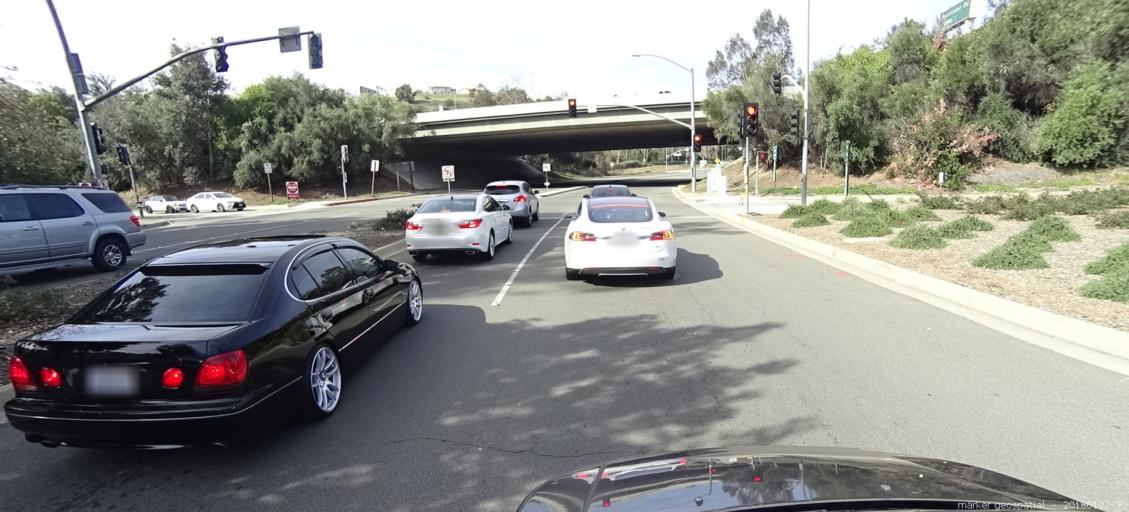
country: US
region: California
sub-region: Los Angeles County
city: Walnut
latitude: 33.9681
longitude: -117.8481
